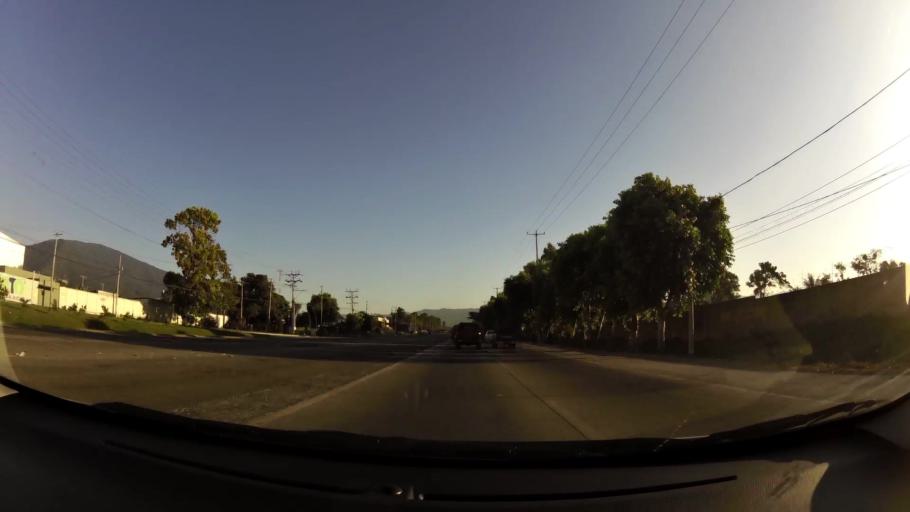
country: SV
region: La Libertad
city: Ciudad Arce
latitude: 13.7723
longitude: -89.3718
